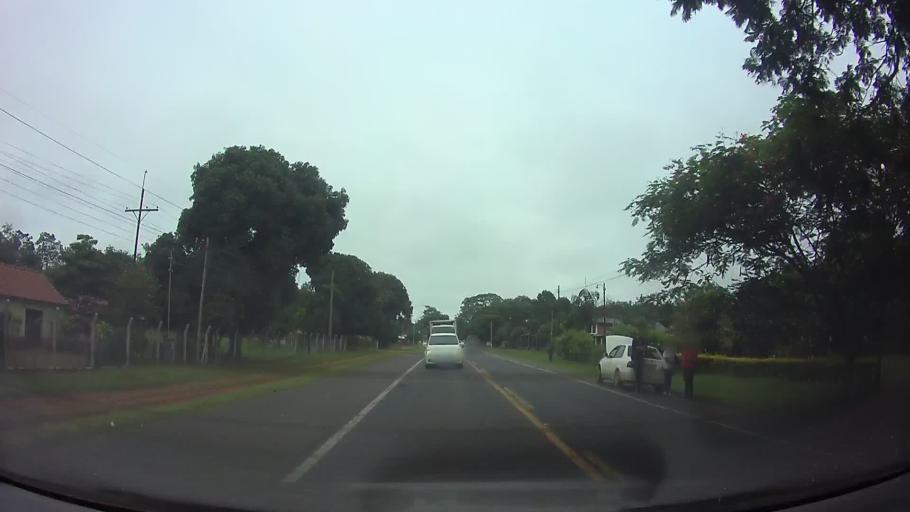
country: PY
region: Paraguari
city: Paraguari
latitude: -25.5996
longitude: -57.2006
